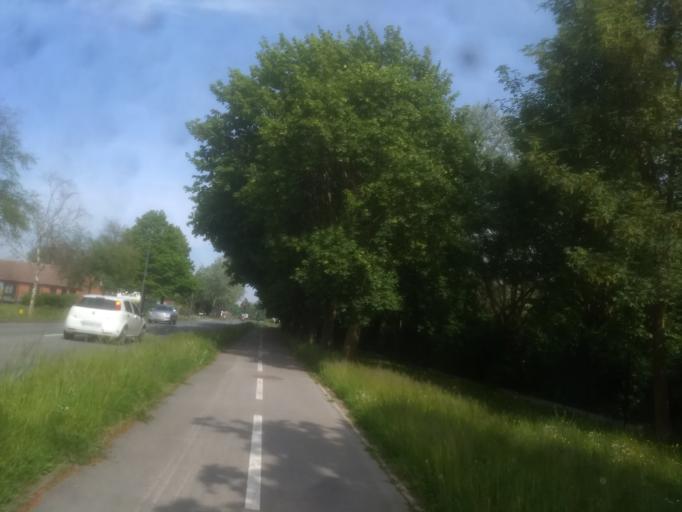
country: FR
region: Nord-Pas-de-Calais
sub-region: Departement du Pas-de-Calais
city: Saint-Laurent-Blangy
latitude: 50.2854
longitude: 2.8112
